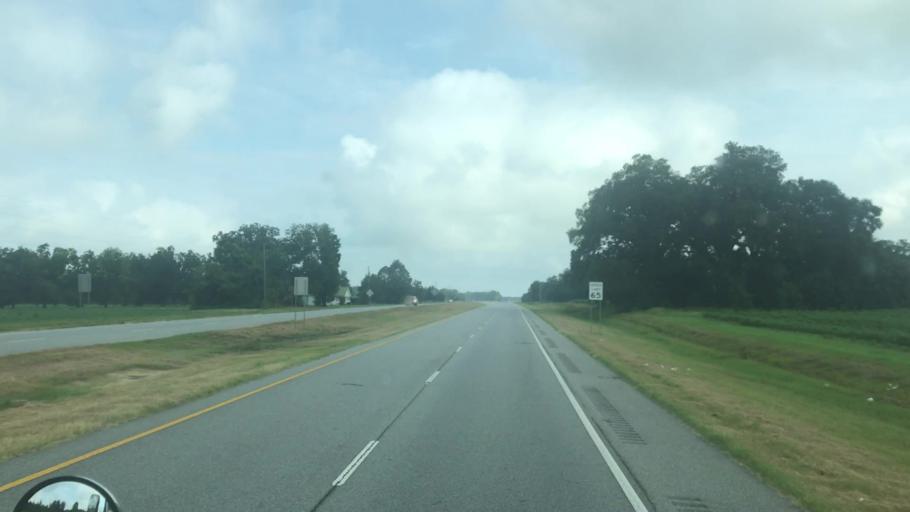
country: US
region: Georgia
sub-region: Miller County
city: Colquitt
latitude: 31.1765
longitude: -84.7601
